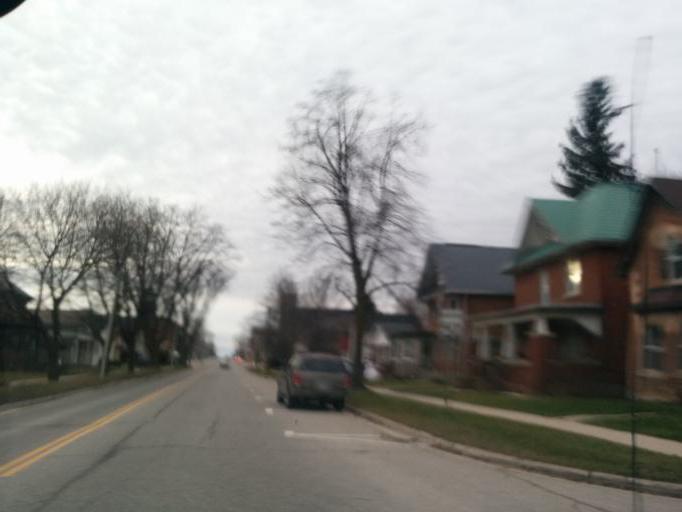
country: CA
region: Ontario
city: Shelburne
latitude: 44.0791
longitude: -80.2010
